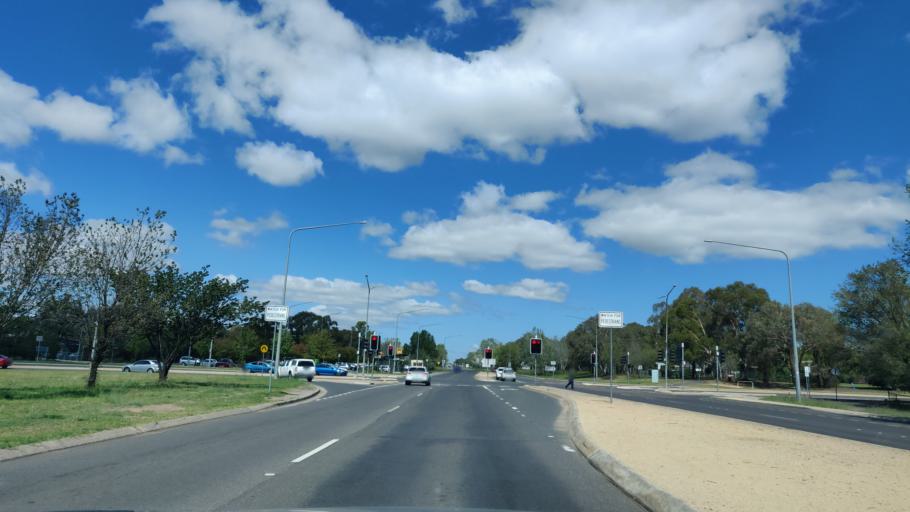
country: AU
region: Australian Capital Territory
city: Macarthur
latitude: -35.3636
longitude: 149.0925
